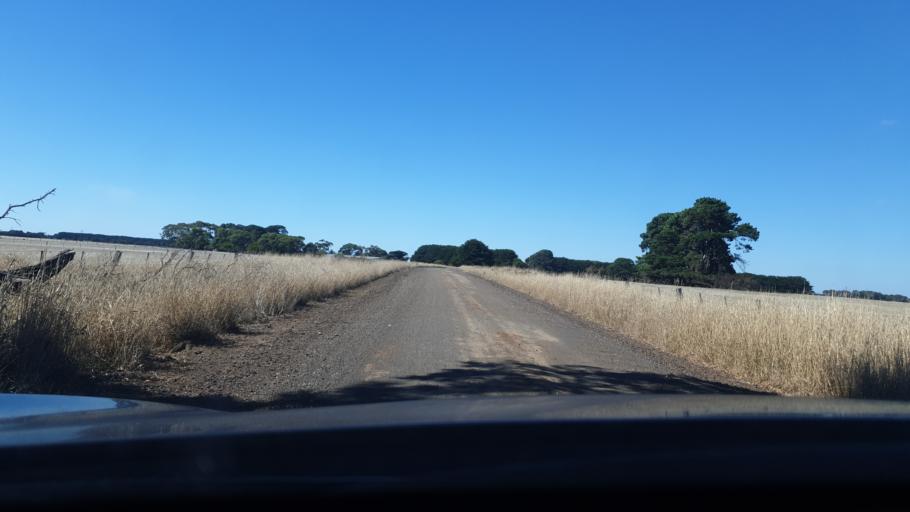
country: AU
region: Victoria
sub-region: Warrnambool
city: Warrnambool
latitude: -38.1656
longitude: 142.3704
